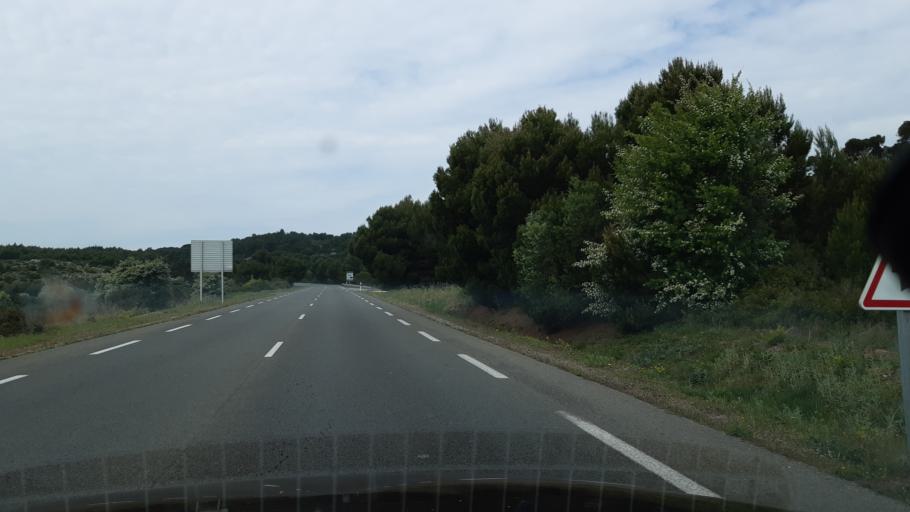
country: FR
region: Languedoc-Roussillon
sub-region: Departement de l'Aude
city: Gruissan
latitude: 43.1188
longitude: 3.0855
